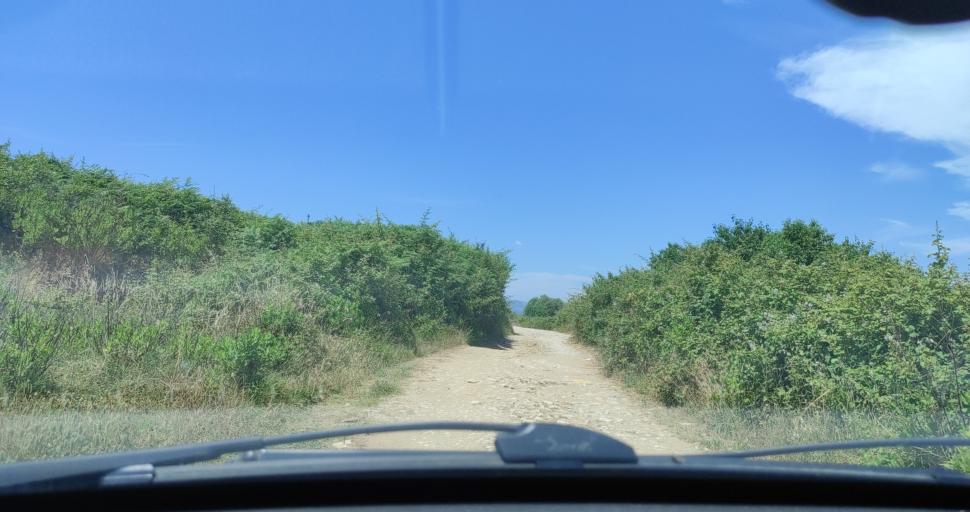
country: AL
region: Shkoder
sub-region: Rrethi i Shkodres
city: Velipoje
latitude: 41.8825
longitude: 19.3922
